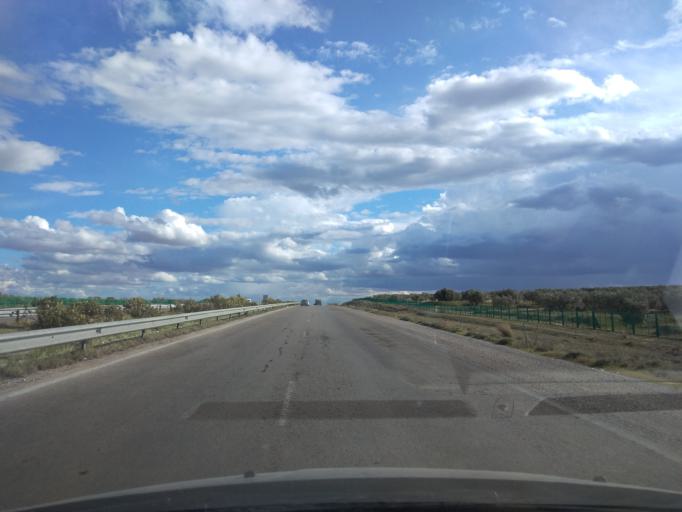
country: TN
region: Al Munastir
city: Manzil Kamil
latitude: 35.5501
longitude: 10.6197
